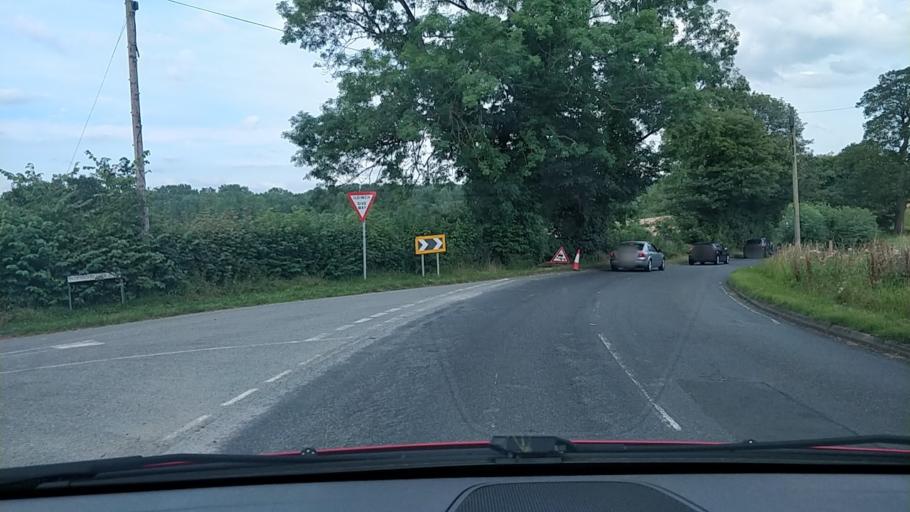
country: GB
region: Wales
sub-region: County of Flintshire
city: Penyffordd
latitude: 53.1427
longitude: -3.0695
